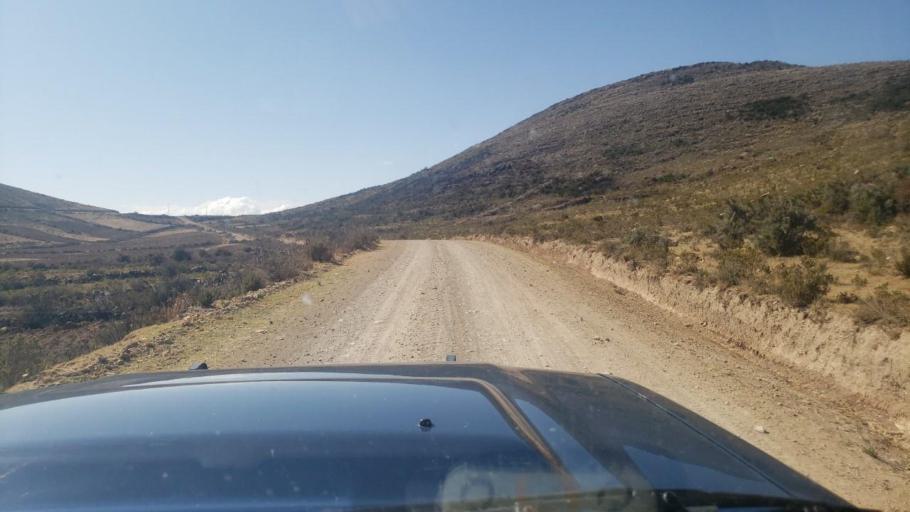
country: BO
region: La Paz
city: Huatajata
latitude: -16.3327
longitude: -68.6923
